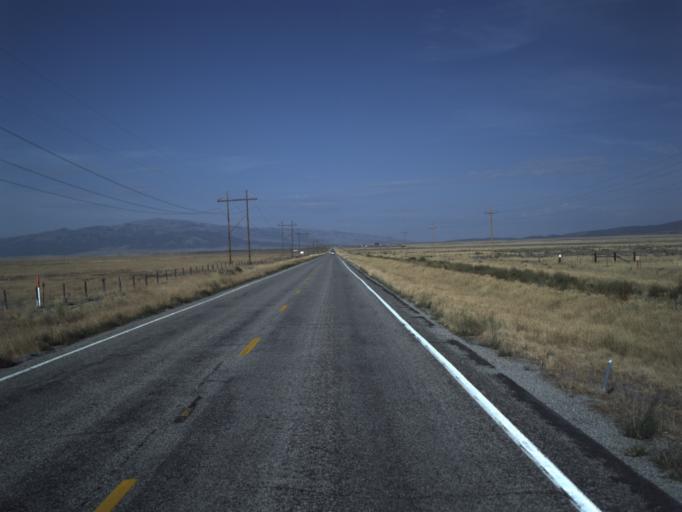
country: US
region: Idaho
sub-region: Oneida County
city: Malad City
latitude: 41.9662
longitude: -112.9498
